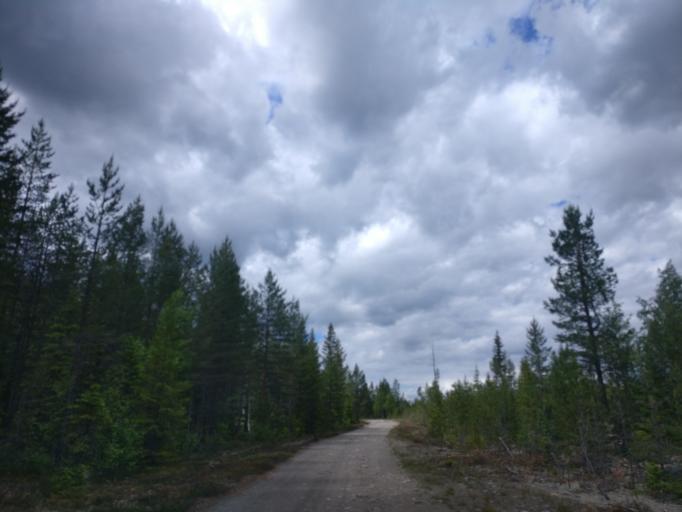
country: SE
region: Jaemtland
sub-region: Harjedalens Kommun
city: Sveg
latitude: 62.1956
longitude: 13.4142
